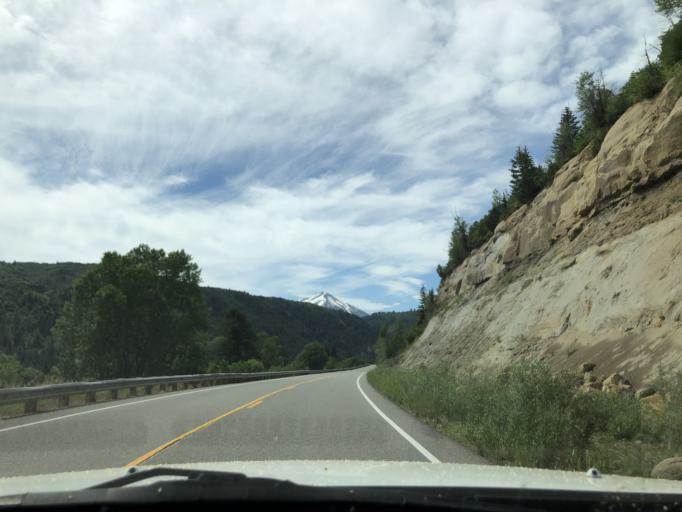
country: US
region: Colorado
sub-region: Delta County
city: Paonia
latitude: 38.9769
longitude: -107.3432
